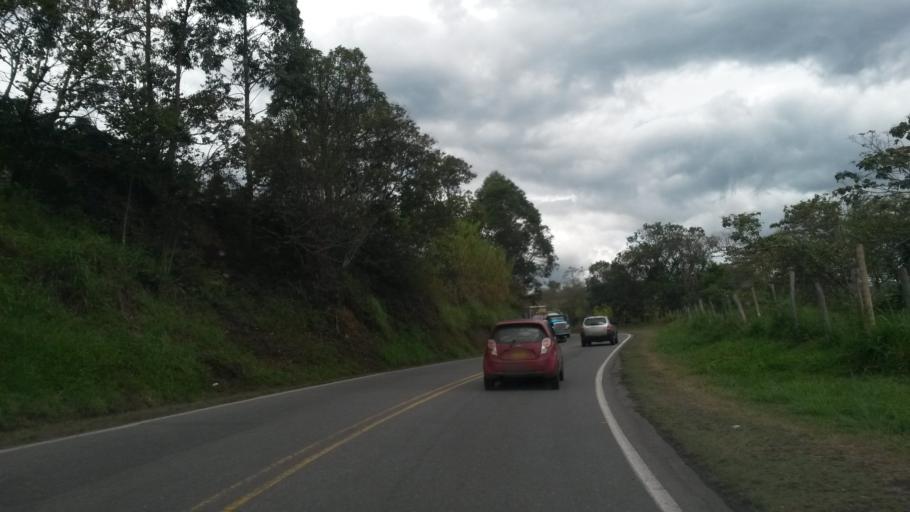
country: CO
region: Cauca
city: Rosas
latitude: 2.3408
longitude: -76.6935
